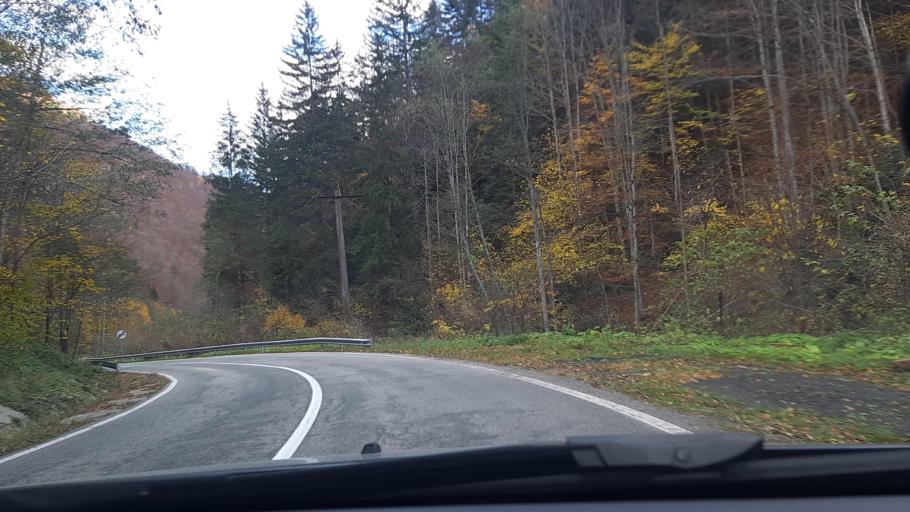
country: RO
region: Valcea
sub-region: Comuna Voineasa
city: Voineasa
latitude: 45.4301
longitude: 23.9006
